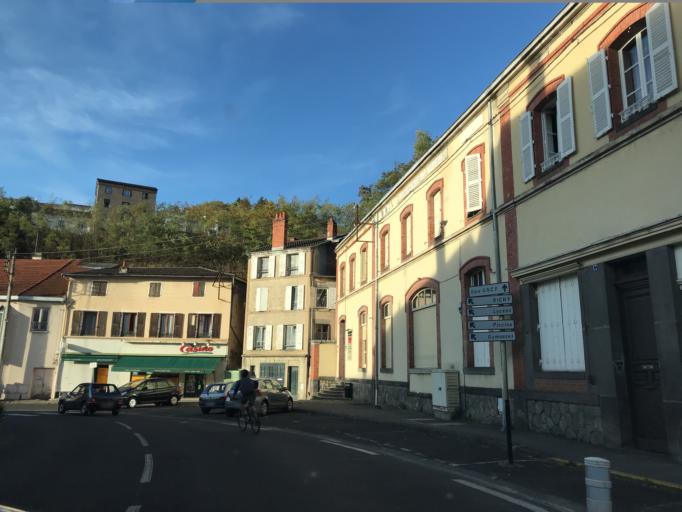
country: FR
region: Auvergne
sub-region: Departement du Puy-de-Dome
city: Thiers
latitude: 45.8598
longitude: 3.5463
